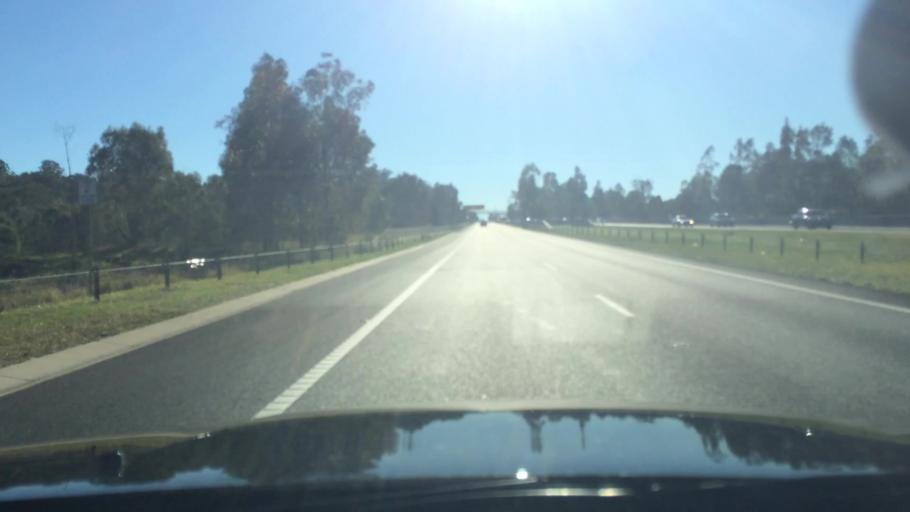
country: AU
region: New South Wales
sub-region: Fairfield
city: Cecil Park
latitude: -33.8859
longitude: 150.8367
